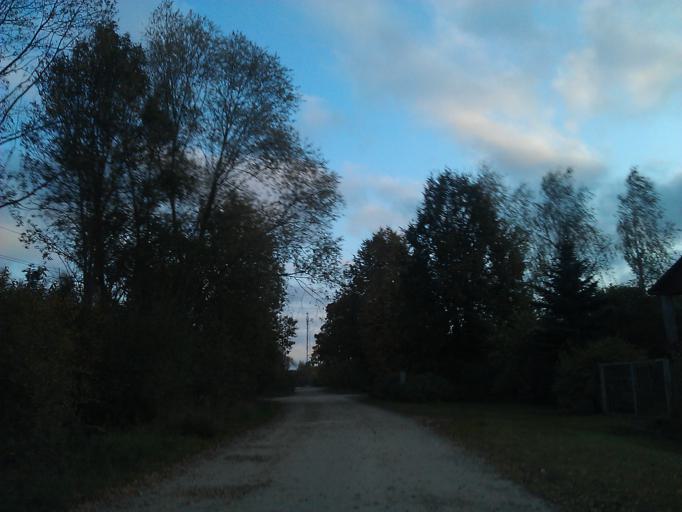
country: LV
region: Adazi
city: Adazi
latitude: 57.0708
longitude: 24.3315
